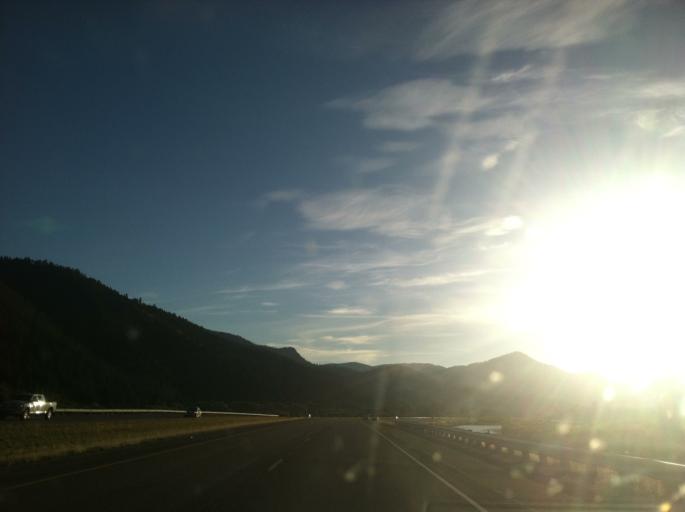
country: US
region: Montana
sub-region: Missoula County
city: Clinton
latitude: 46.7001
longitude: -113.3895
